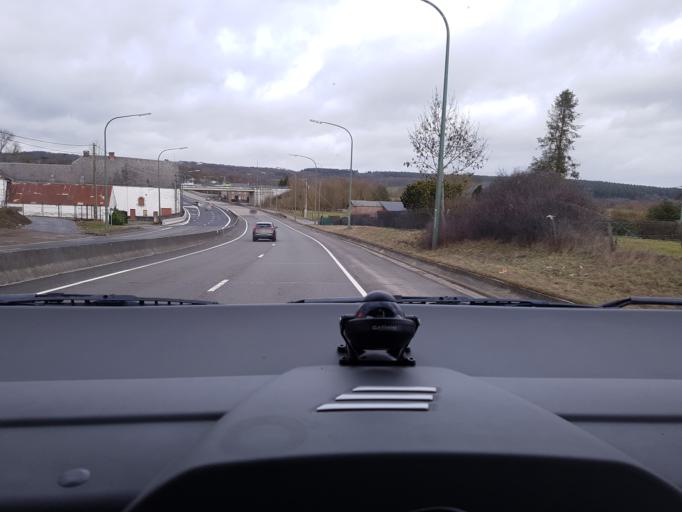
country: BE
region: Wallonia
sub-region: Province du Luxembourg
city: Marche-en-Famenne
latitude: 50.2478
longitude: 5.2841
